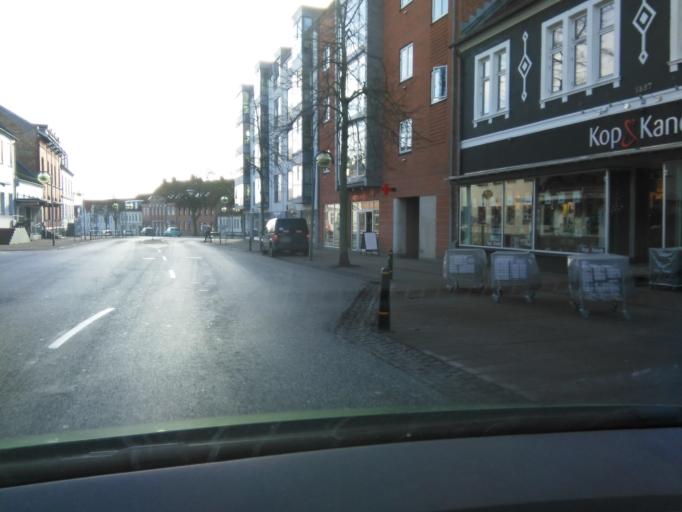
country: DK
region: Central Jutland
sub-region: Skanderborg Kommune
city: Skanderborg
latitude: 56.0327
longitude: 9.9323
